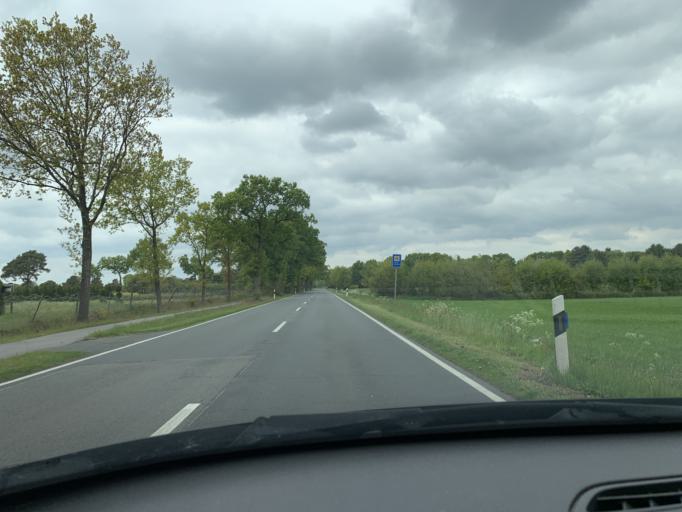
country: DE
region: Lower Saxony
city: Bad Zwischenahn
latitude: 53.1854
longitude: 8.0625
